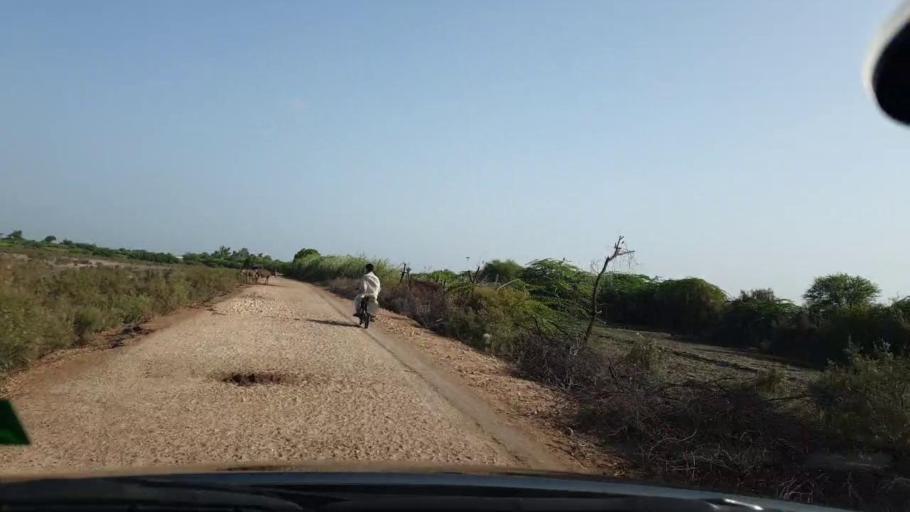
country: PK
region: Sindh
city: Tando Bago
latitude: 24.6555
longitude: 69.0414
